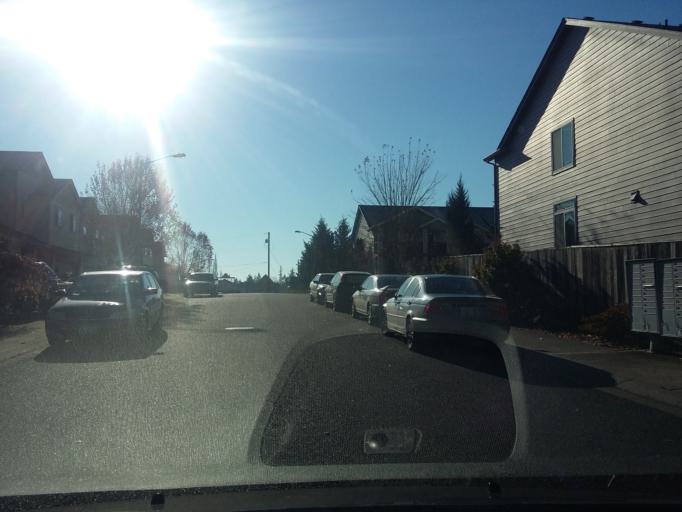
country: US
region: Washington
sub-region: Clark County
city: Barberton
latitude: 45.6907
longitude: -122.6235
